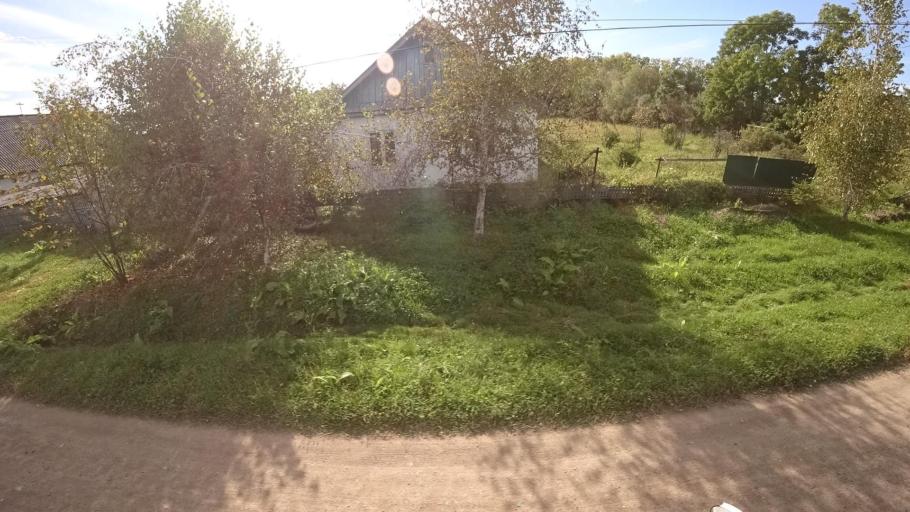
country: RU
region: Primorskiy
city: Dostoyevka
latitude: 44.2994
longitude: 133.4599
